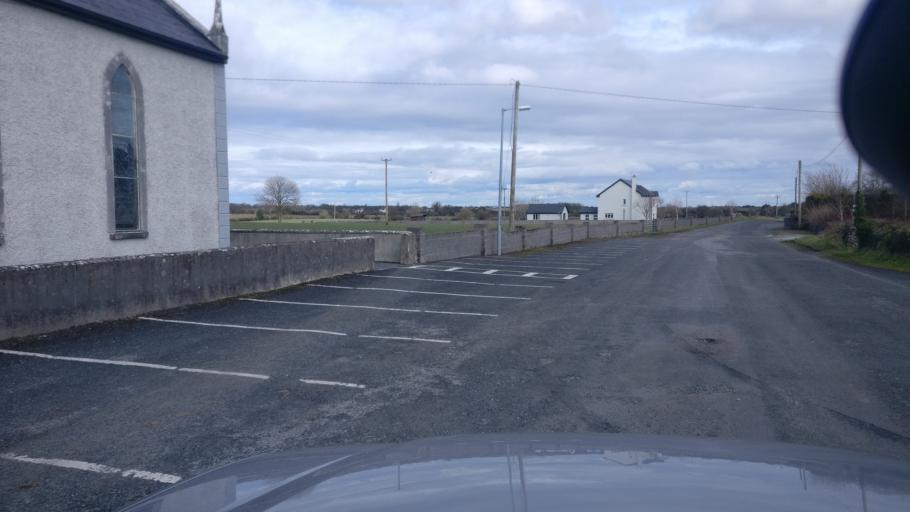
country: IE
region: Connaught
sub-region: County Galway
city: Loughrea
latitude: 53.1915
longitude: -8.4807
